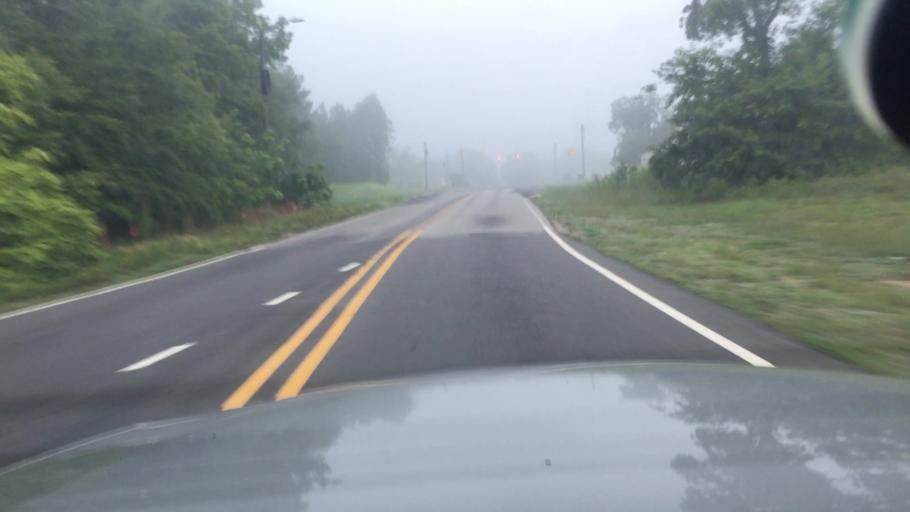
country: US
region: North Carolina
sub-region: Cumberland County
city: Fayetteville
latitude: 35.0148
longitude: -78.9079
